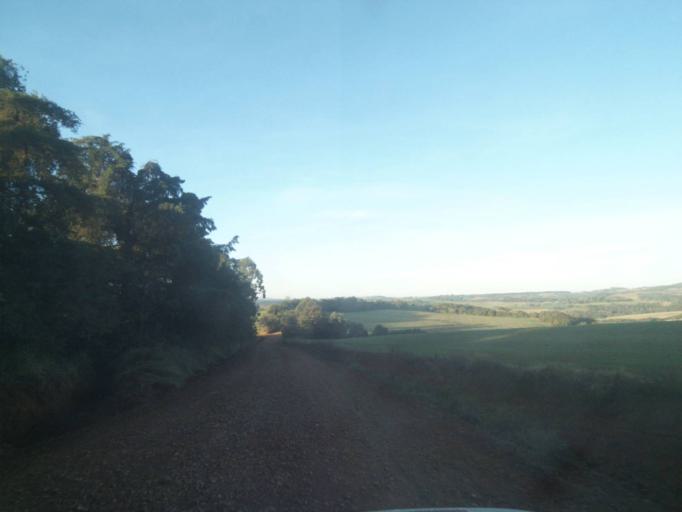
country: BR
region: Parana
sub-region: Tibagi
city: Tibagi
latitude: -24.5352
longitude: -50.5234
